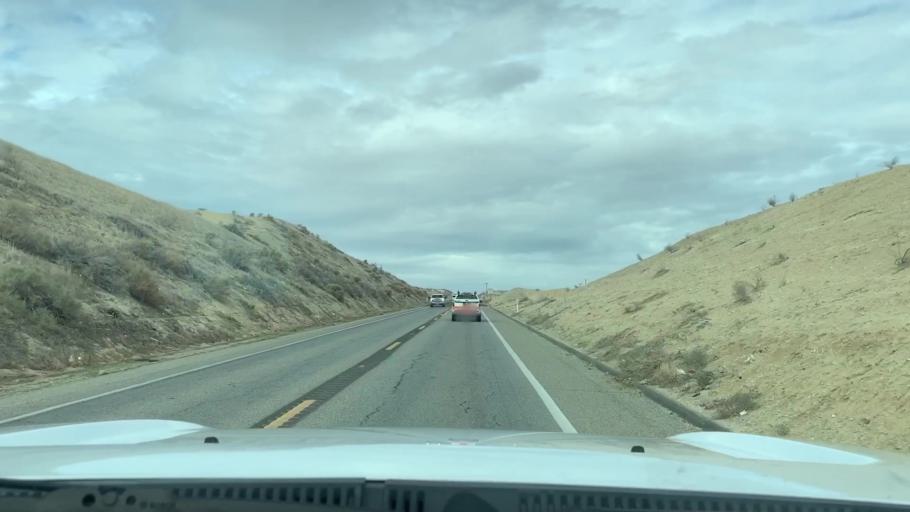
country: US
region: California
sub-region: Kern County
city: Maricopa
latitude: 35.0981
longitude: -119.4129
